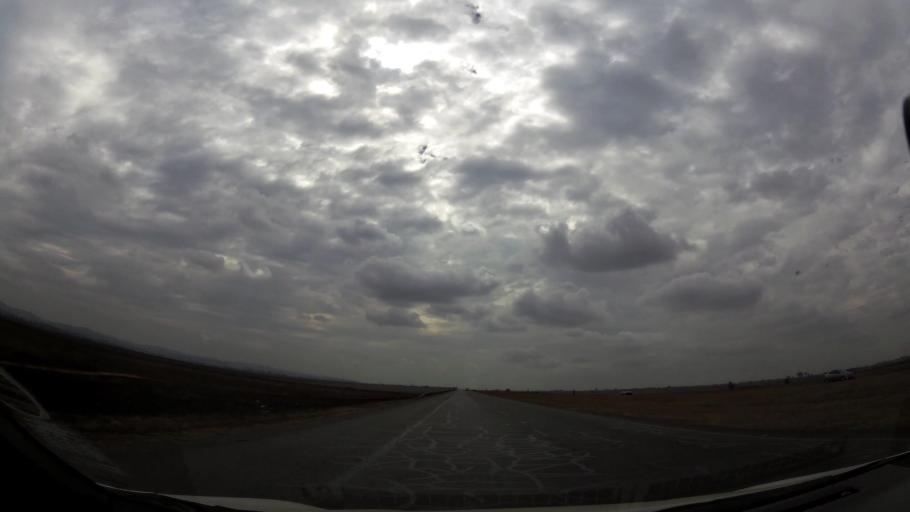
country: ZA
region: Gauteng
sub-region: Ekurhuleni Metropolitan Municipality
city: Germiston
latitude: -26.3836
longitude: 28.0870
